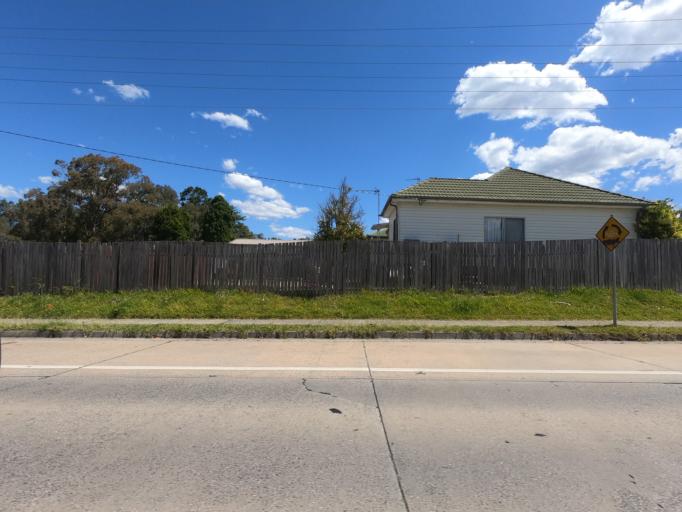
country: AU
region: New South Wales
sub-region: Wollongong
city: East Corrimal
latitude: -34.3773
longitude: 150.9085
